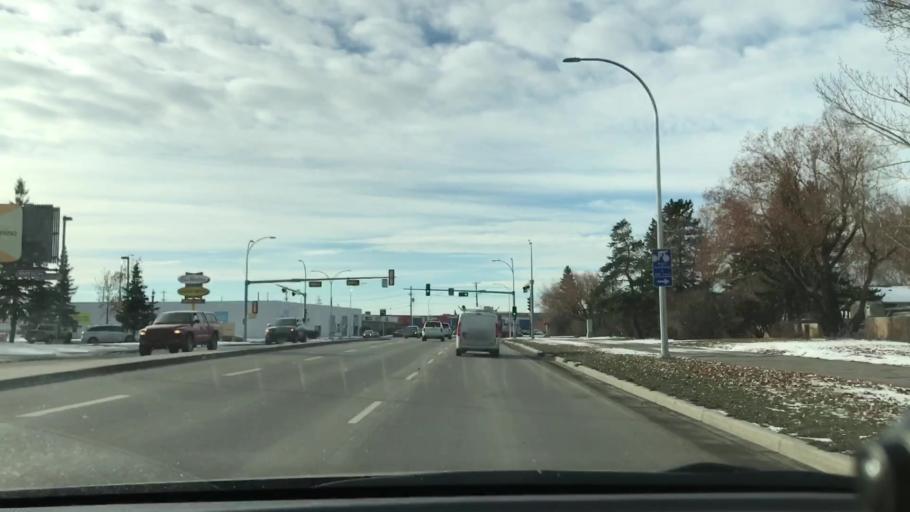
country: CA
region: Alberta
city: Edmonton
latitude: 53.5011
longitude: -113.4574
